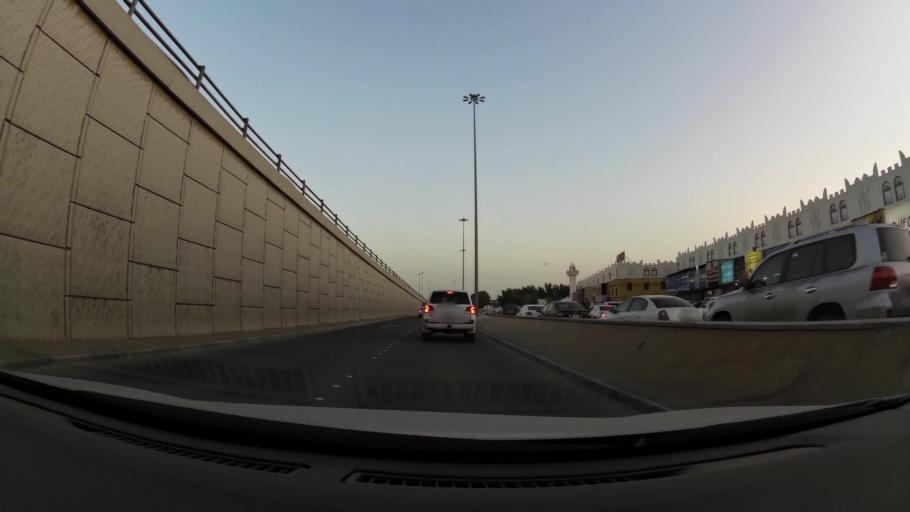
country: QA
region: Baladiyat ar Rayyan
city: Ar Rayyan
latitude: 25.3185
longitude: 51.4703
